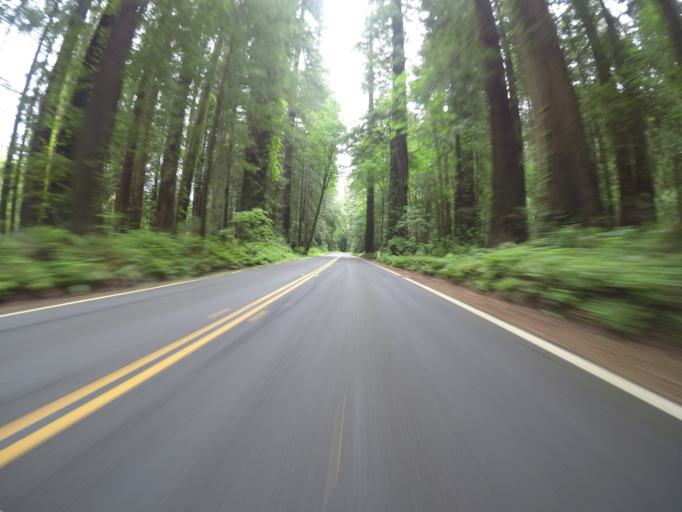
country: US
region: California
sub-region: Humboldt County
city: Rio Dell
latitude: 40.4445
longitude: -124.0187
